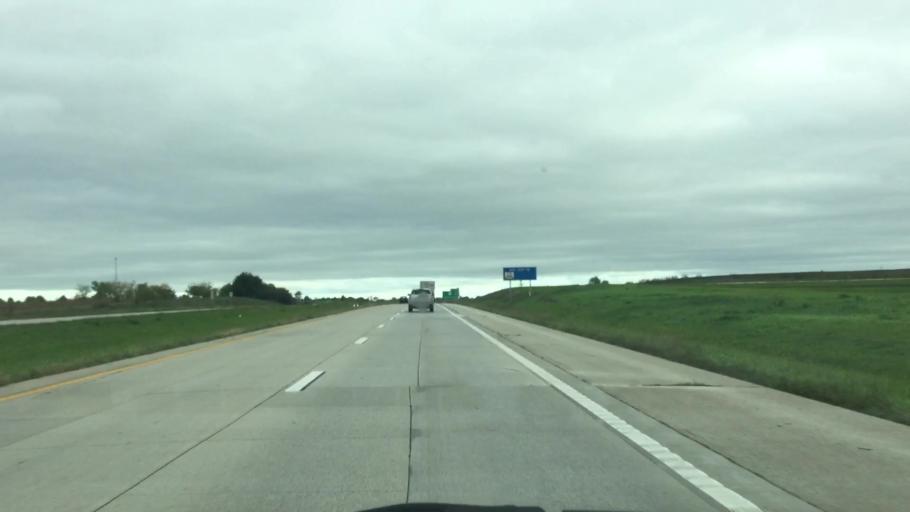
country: US
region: Missouri
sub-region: Daviess County
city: Gallatin
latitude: 40.0690
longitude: -94.0936
